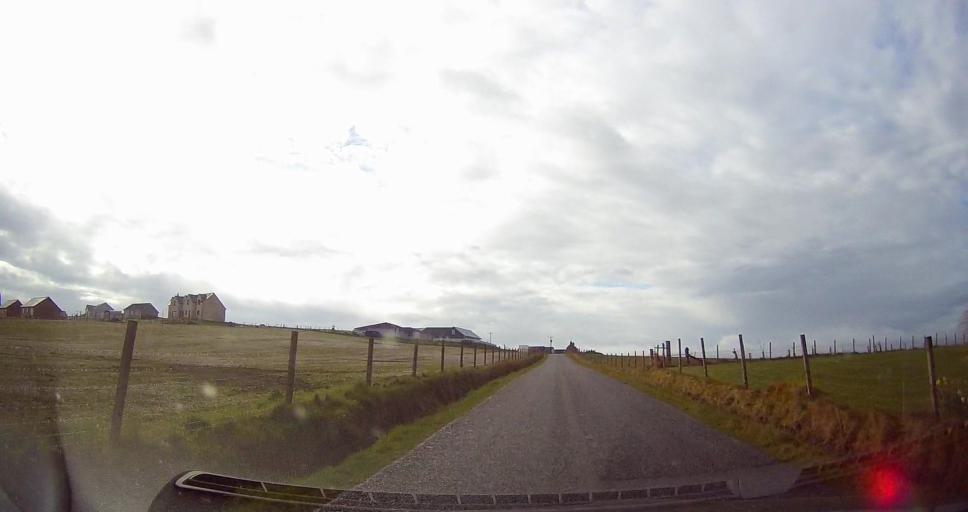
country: GB
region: Scotland
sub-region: Shetland Islands
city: Sandwick
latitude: 60.0590
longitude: -1.2143
